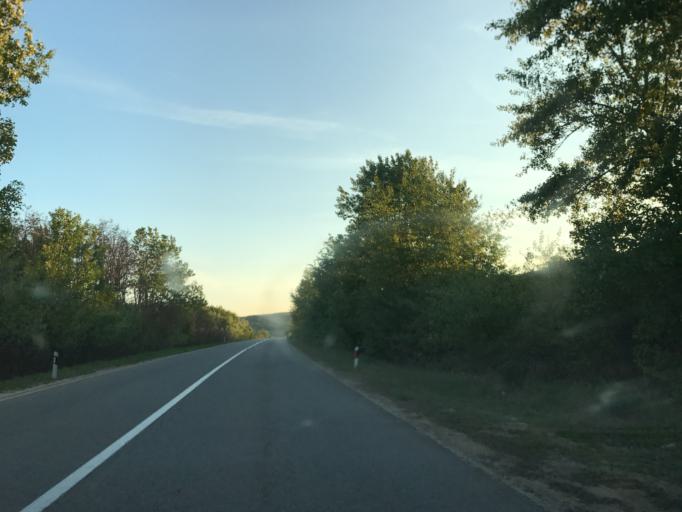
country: RO
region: Mehedinti
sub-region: Comuna Gogosu
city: Ostrovu Mare
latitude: 44.4073
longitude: 22.4810
